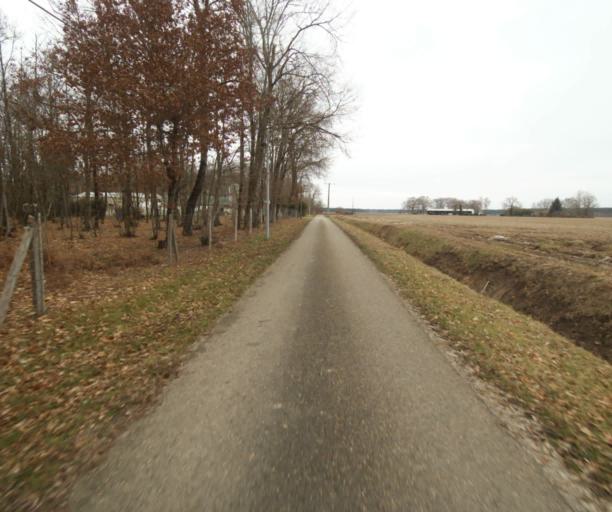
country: FR
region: Aquitaine
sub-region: Departement des Landes
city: Gabarret
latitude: 44.0135
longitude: -0.0128
